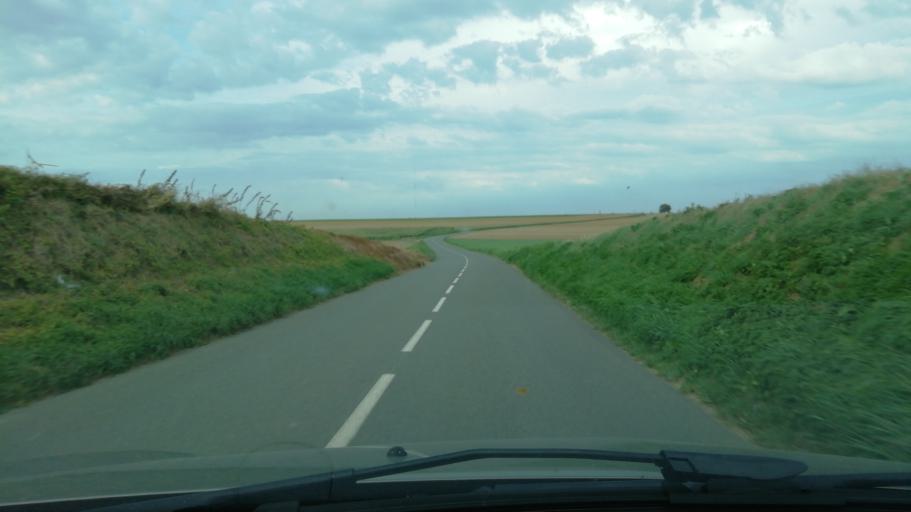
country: FR
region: Nord-Pas-de-Calais
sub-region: Departement du Nord
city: Avesnes-les-Aubert
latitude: 50.1721
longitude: 3.3822
